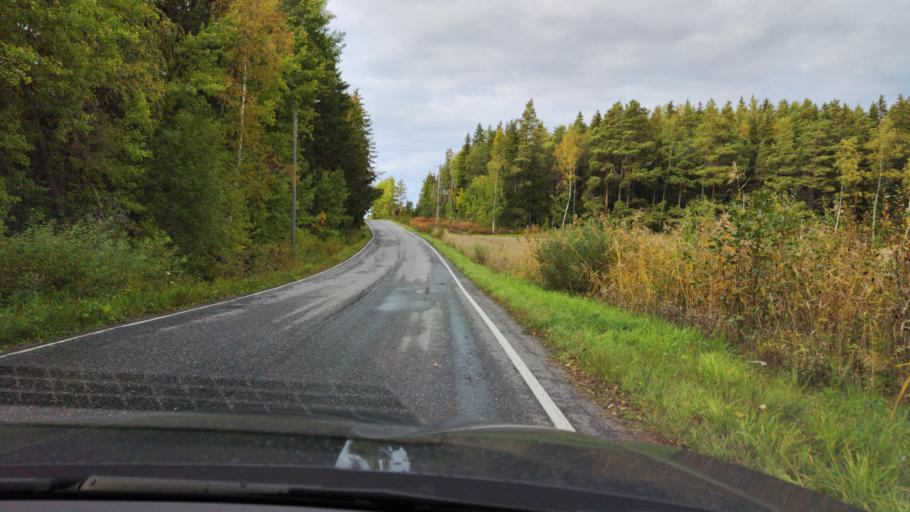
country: FI
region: Varsinais-Suomi
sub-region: Aboland-Turunmaa
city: Pargas
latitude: 60.3515
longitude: 22.1823
